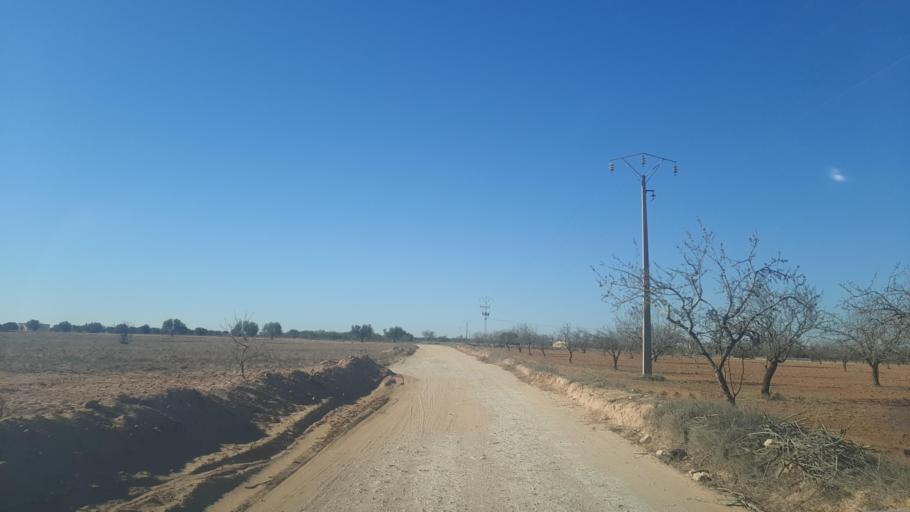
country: TN
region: Safaqis
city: Sfax
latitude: 34.8879
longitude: 10.5876
